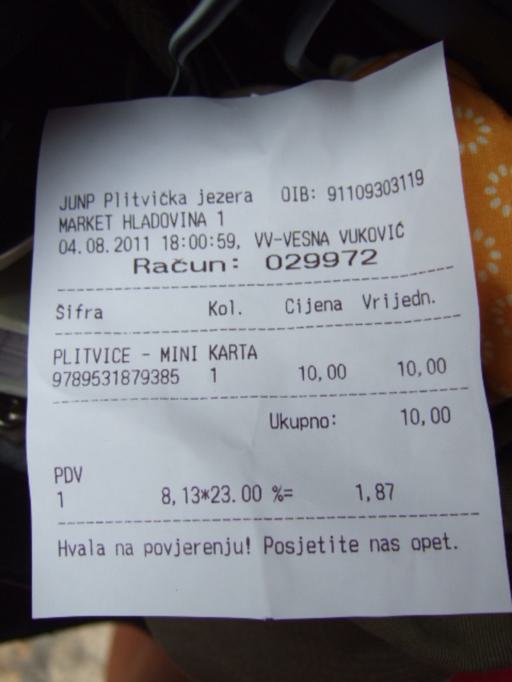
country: HR
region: Licko-Senjska
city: Jezerce
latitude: 44.8830
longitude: 15.6234
